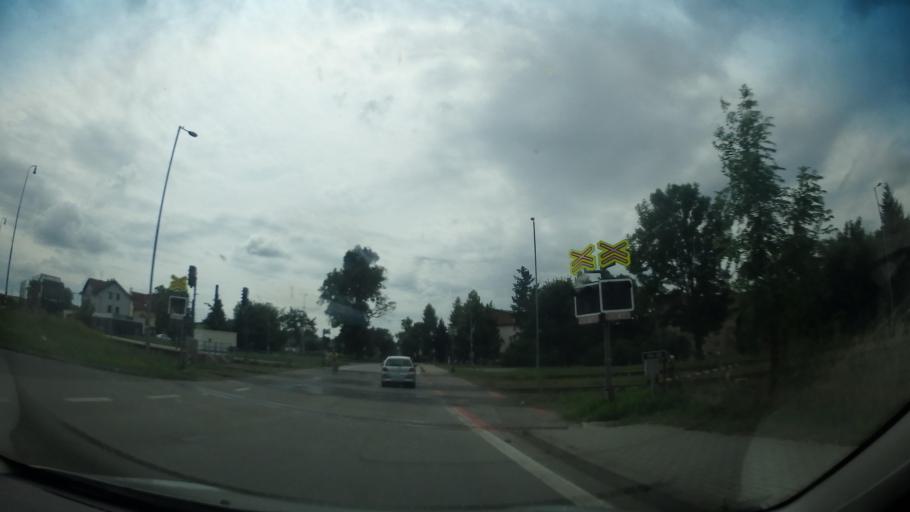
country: CZ
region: Vysocina
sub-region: Okres Zd'ar nad Sazavou
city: Nove Mesto na Morave
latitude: 49.5694
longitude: 16.0793
